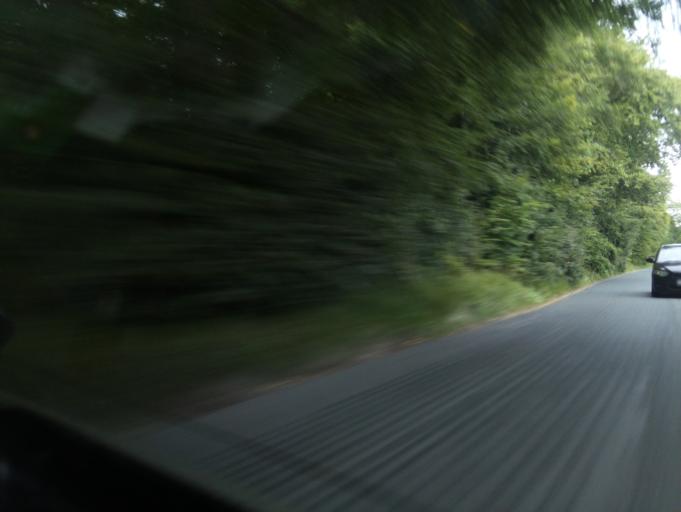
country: GB
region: England
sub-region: Gloucestershire
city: Painswick
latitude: 51.8159
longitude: -2.1697
